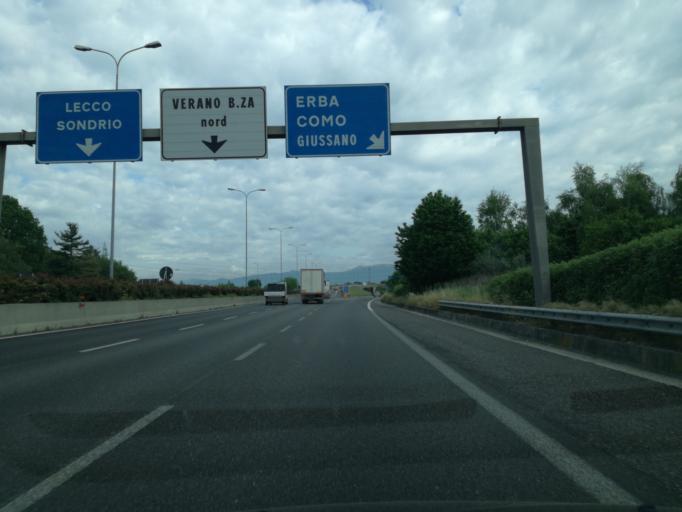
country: IT
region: Lombardy
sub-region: Provincia di Monza e Brianza
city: Verano Brianza
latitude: 45.6814
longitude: 9.2172
